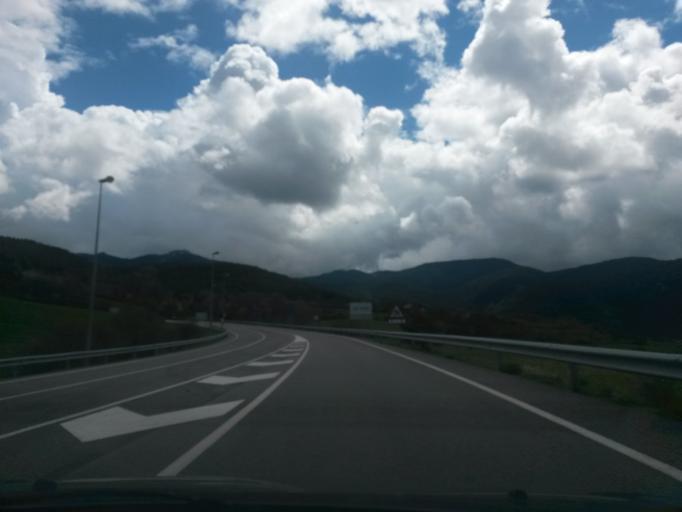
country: ES
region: Catalonia
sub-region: Provincia de Girona
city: Isovol
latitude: 42.3613
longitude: 1.8132
